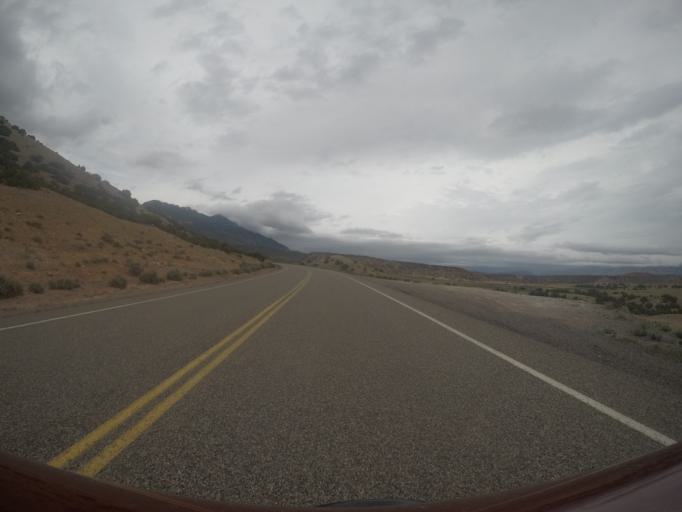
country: US
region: Wyoming
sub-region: Big Horn County
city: Lovell
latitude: 45.0704
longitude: -108.2547
